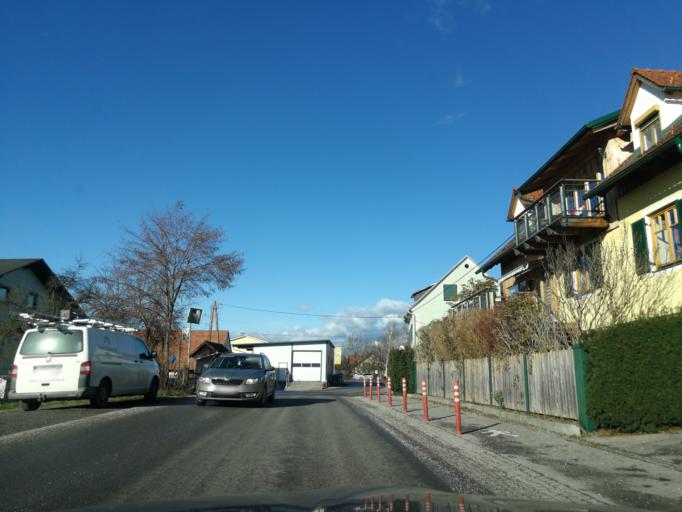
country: AT
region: Styria
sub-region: Politischer Bezirk Weiz
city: Hofstatten an der Raab
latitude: 47.0751
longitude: 15.7469
